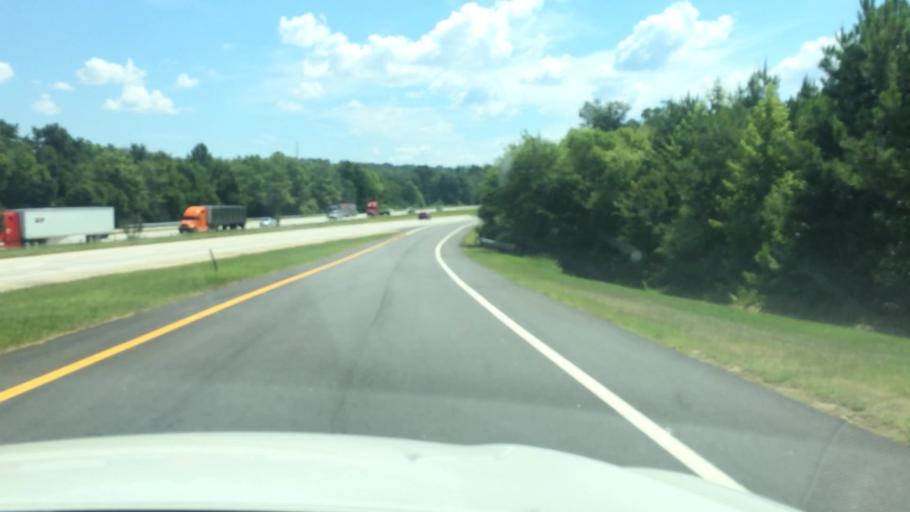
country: US
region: South Carolina
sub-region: Aiken County
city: Belvedere
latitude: 33.5405
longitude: -81.9892
